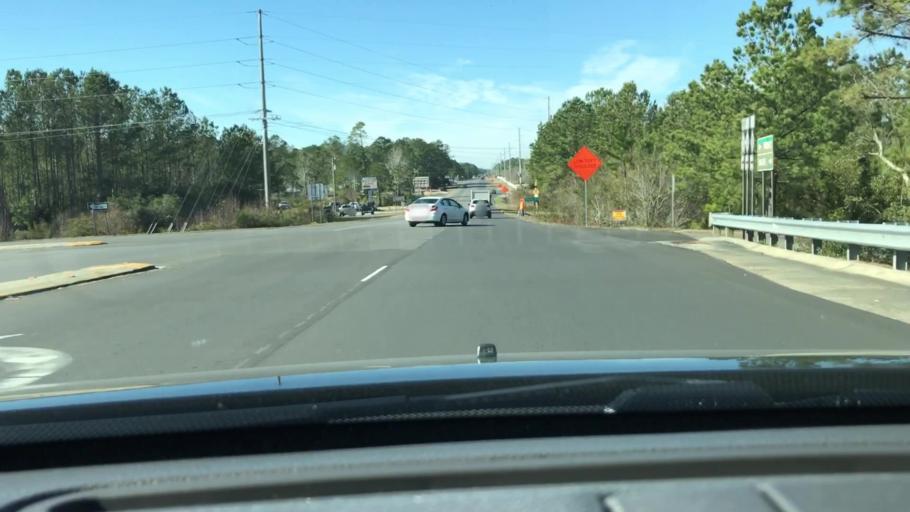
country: US
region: North Carolina
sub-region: Brunswick County
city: Shallotte
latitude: 33.9771
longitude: -78.4064
